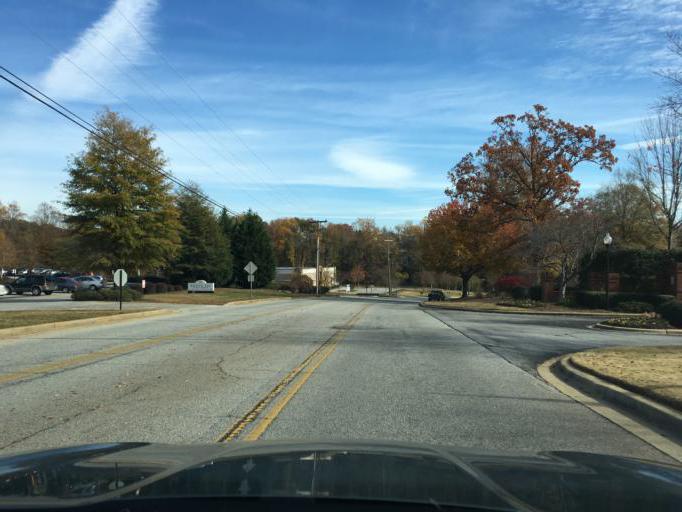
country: US
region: South Carolina
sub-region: Greenville County
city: Wade Hampton
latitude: 34.8537
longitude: -82.3418
